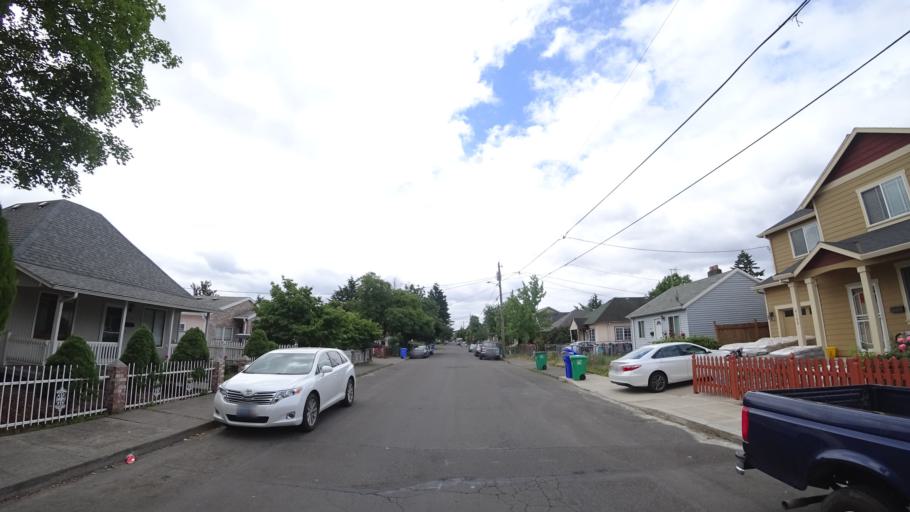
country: US
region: Oregon
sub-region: Multnomah County
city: Lents
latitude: 45.4787
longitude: -122.5770
